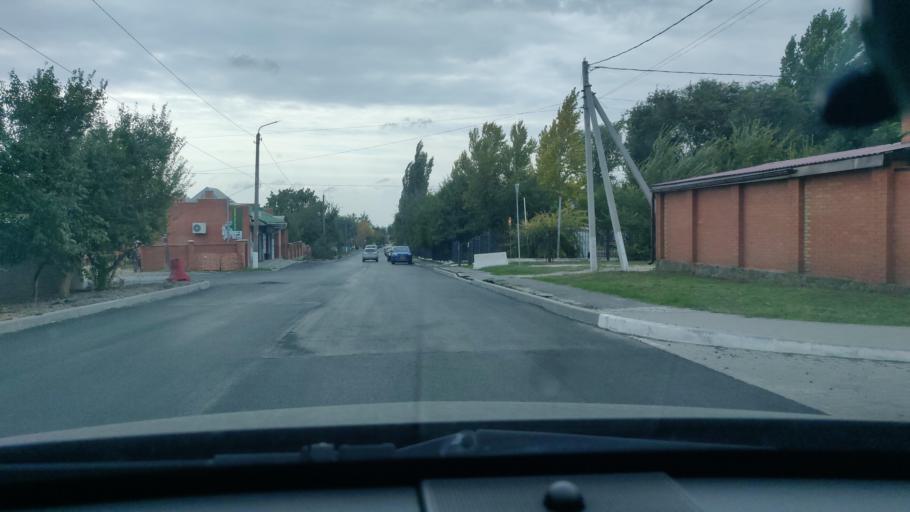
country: RU
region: Rostov
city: Ust'-Donetskiy
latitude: 47.6448
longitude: 40.8731
